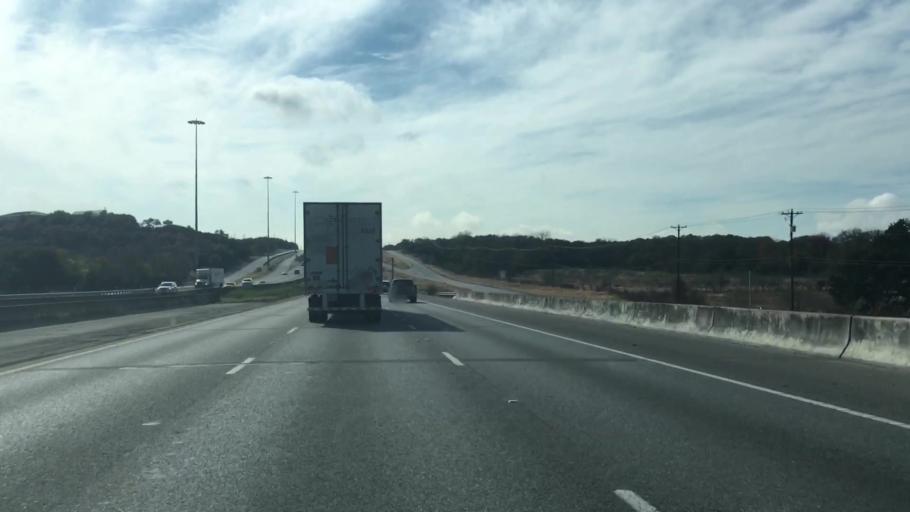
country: US
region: Texas
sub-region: Travis County
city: Onion Creek
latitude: 30.1348
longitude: -97.7983
